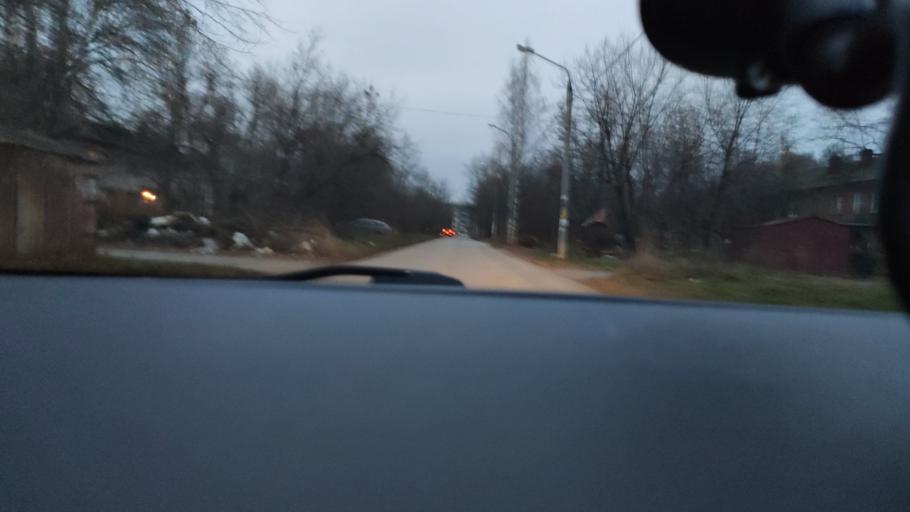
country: RU
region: Perm
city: Perm
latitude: 57.9606
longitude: 56.2354
